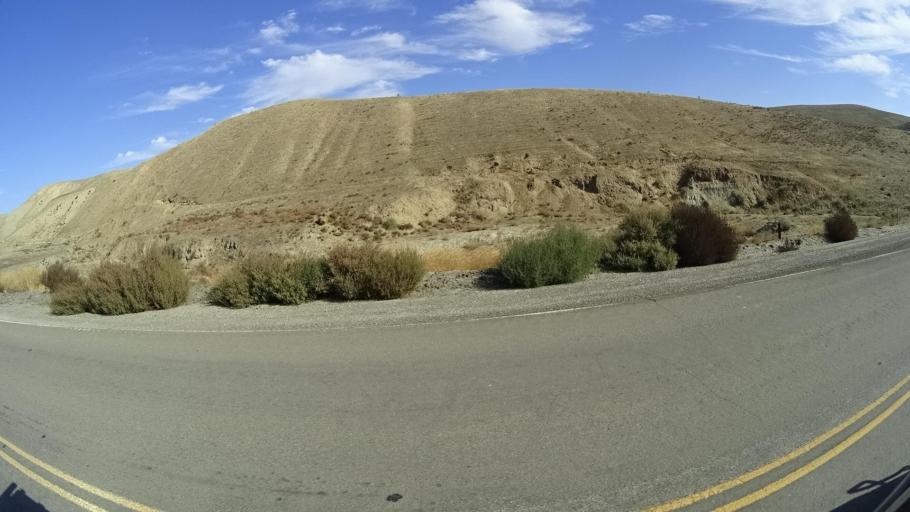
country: US
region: California
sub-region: Kern County
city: Oildale
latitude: 35.5429
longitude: -118.9585
